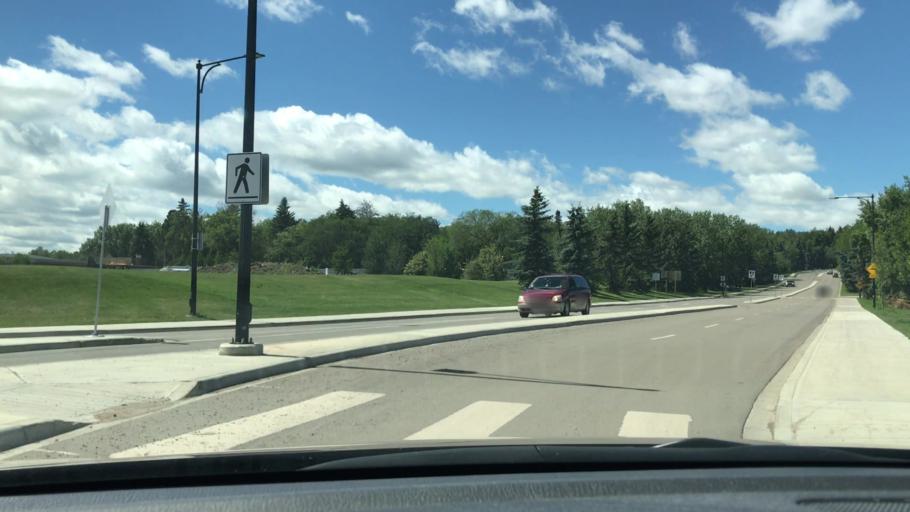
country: CA
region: Alberta
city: Edmonton
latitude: 53.5124
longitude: -113.5504
